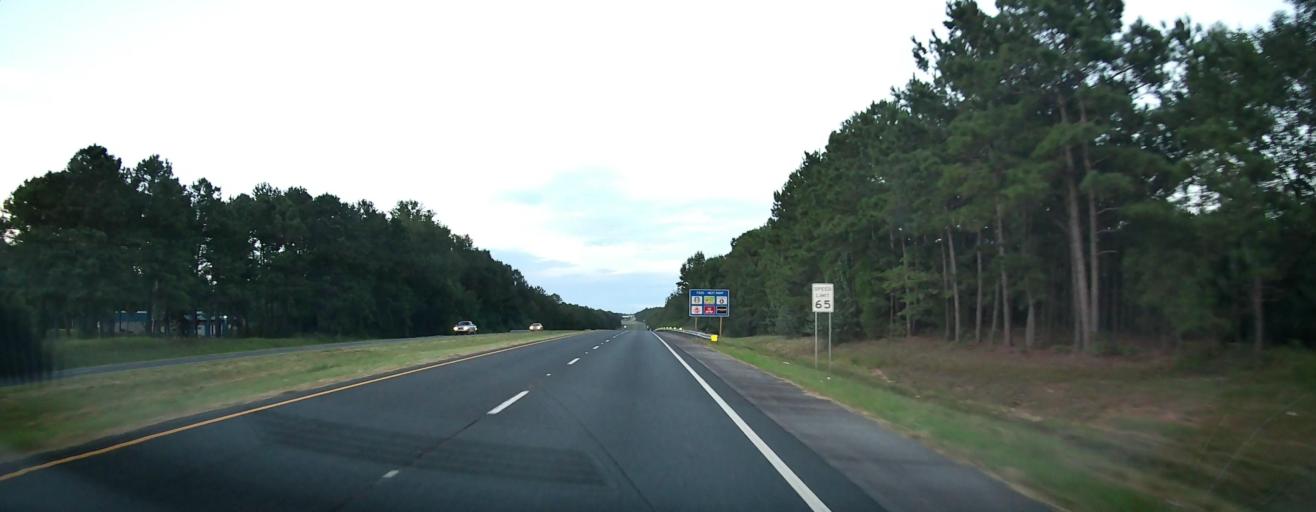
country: US
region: Georgia
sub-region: Muscogee County
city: Columbus
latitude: 32.5280
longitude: -84.8854
